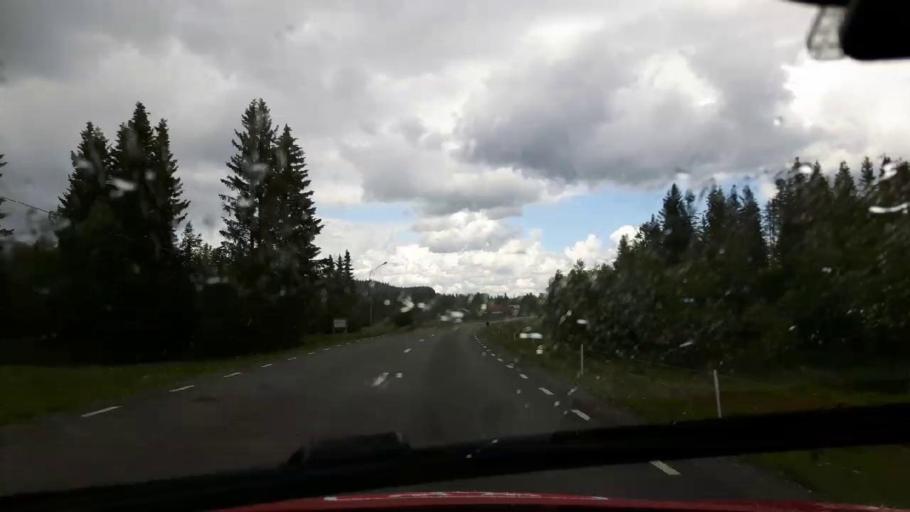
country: SE
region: Jaemtland
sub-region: Krokoms Kommun
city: Krokom
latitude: 63.7460
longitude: 14.2867
